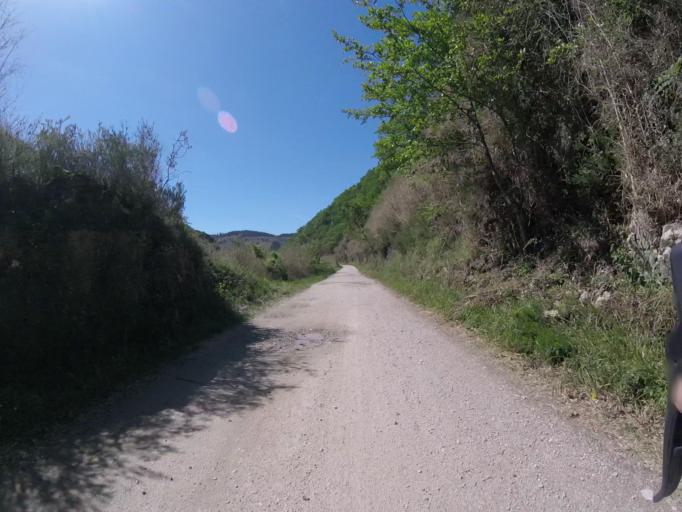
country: ES
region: Navarre
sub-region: Provincia de Navarra
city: Bera
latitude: 43.2882
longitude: -1.7126
